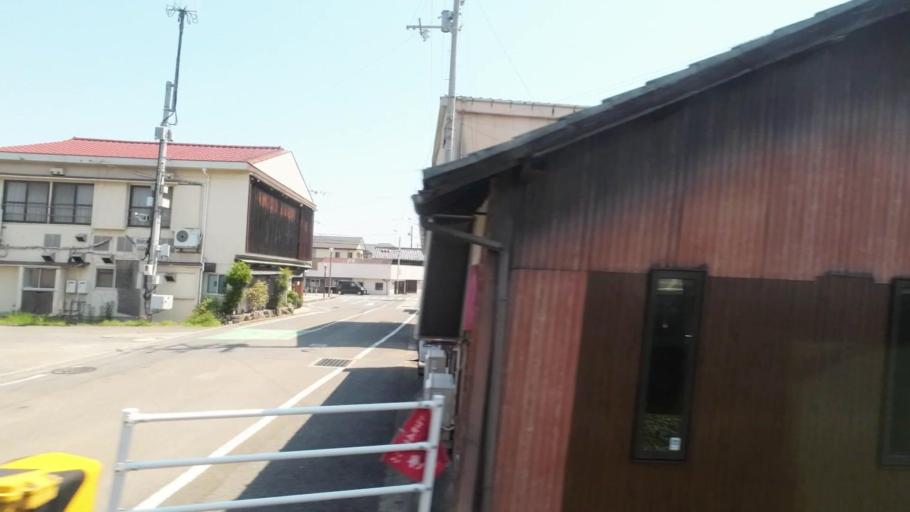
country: JP
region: Ehime
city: Saijo
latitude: 33.9340
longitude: 133.0818
